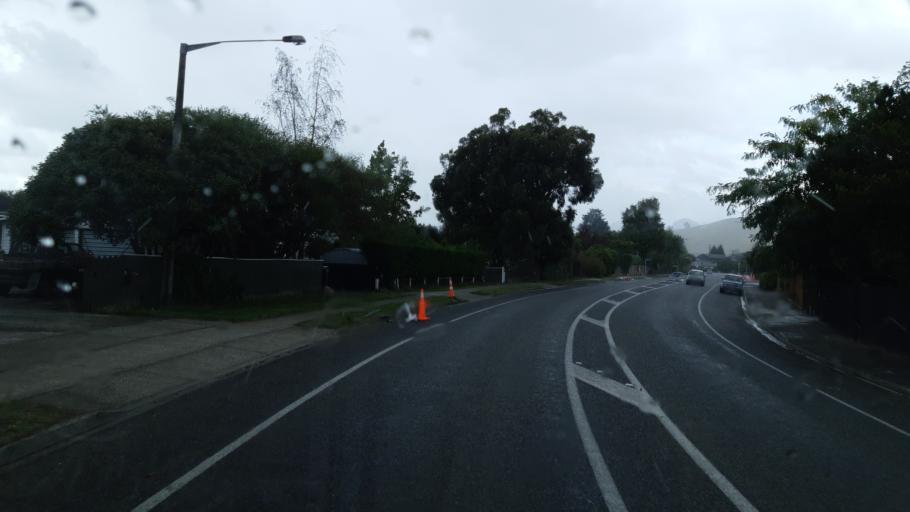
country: NZ
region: Tasman
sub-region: Tasman District
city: Wakefield
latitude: -41.4043
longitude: 173.0464
